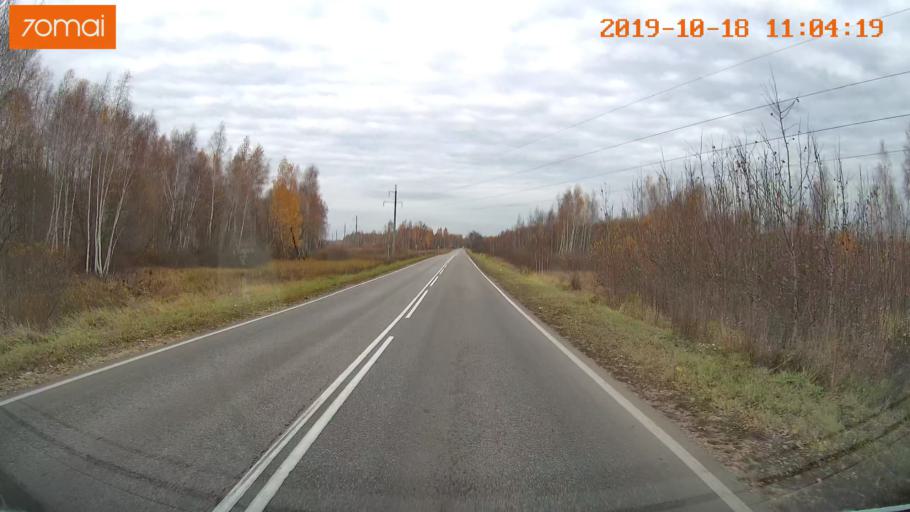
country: RU
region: Tula
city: Yepifan'
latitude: 53.8923
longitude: 38.5496
